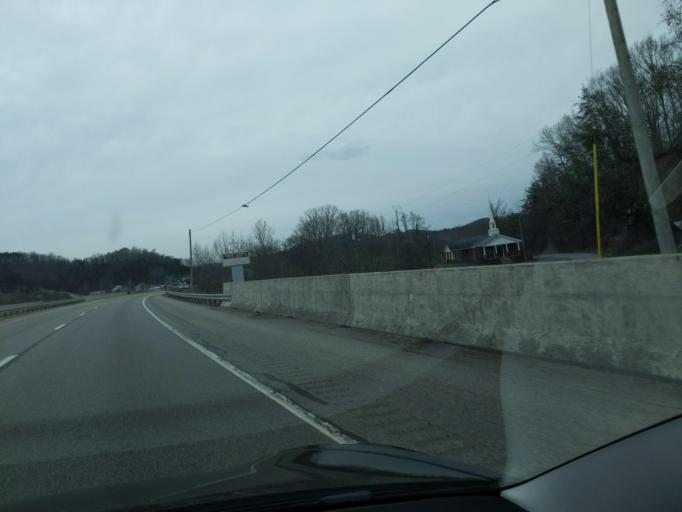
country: US
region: Kentucky
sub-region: Knox County
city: Barbourville
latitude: 36.8624
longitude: -83.7956
